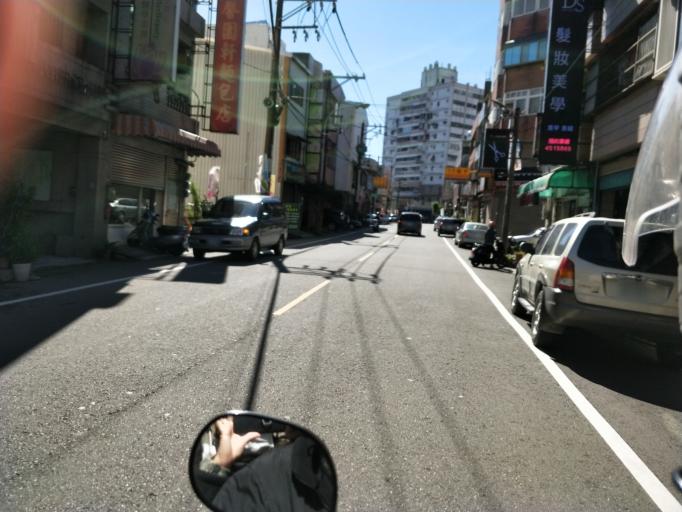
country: TW
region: Taiwan
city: Taoyuan City
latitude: 24.9663
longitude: 121.2298
